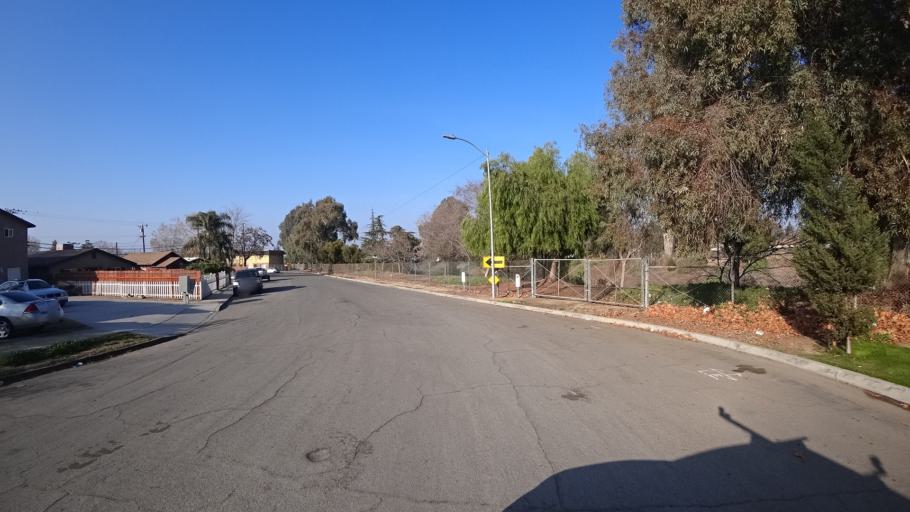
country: US
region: California
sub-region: Kern County
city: Bakersfield
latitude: 35.3843
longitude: -118.9911
